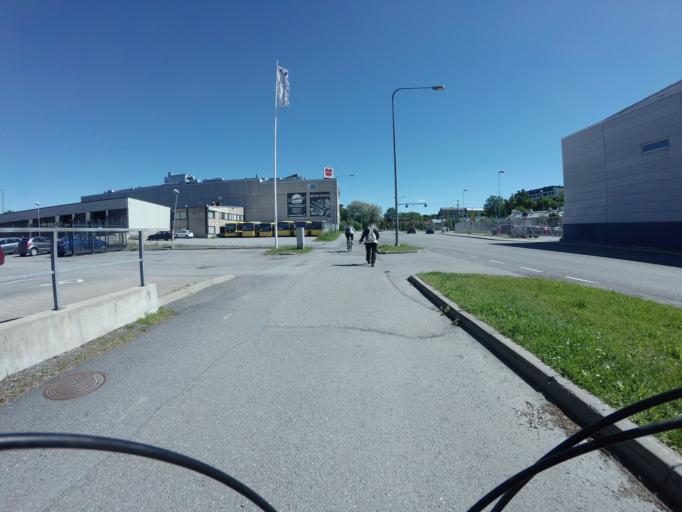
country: FI
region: Varsinais-Suomi
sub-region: Turku
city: Turku
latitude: 60.4493
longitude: 22.2411
